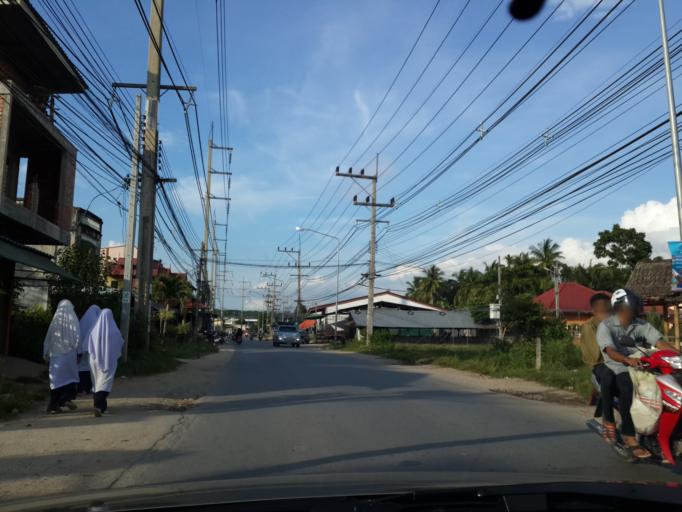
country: TH
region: Yala
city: Yala
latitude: 6.5049
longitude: 101.2692
